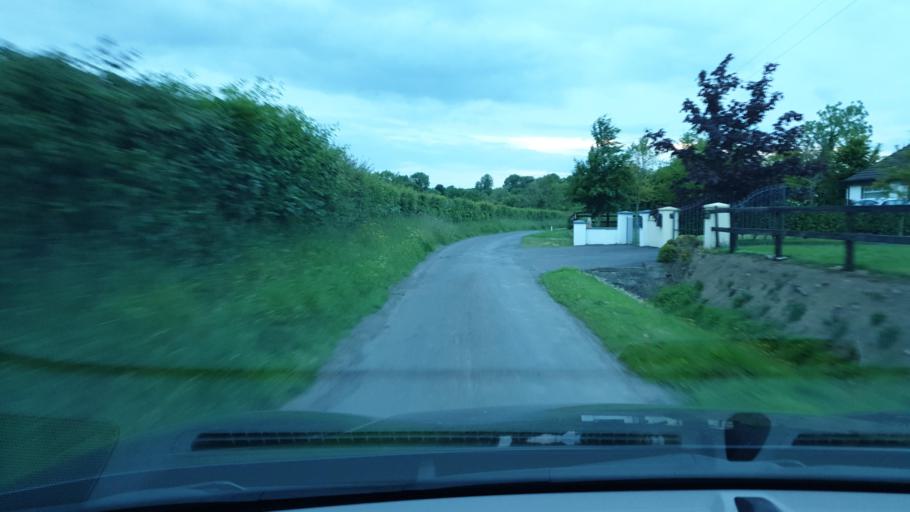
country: IE
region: Leinster
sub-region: An Mhi
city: Ashbourne
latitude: 53.5865
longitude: -6.3657
